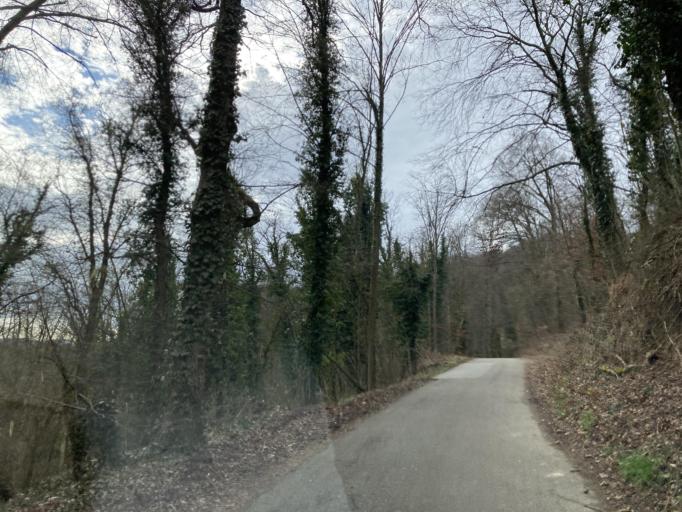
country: DE
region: Baden-Wuerttemberg
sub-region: Freiburg Region
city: Endingen
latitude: 48.1241
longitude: 7.7101
